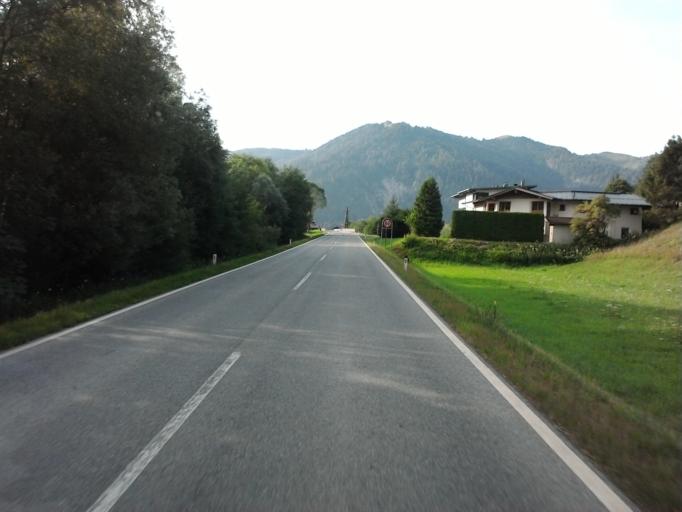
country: AT
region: Tyrol
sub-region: Politischer Bezirk Kitzbuhel
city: Kirchdorf in Tirol
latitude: 47.5848
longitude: 12.4727
